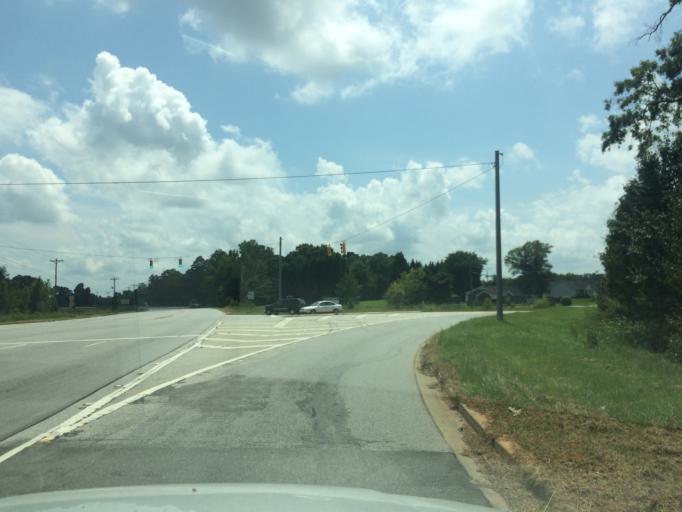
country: US
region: South Carolina
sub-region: Spartanburg County
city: Duncan
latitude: 34.8529
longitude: -82.1476
